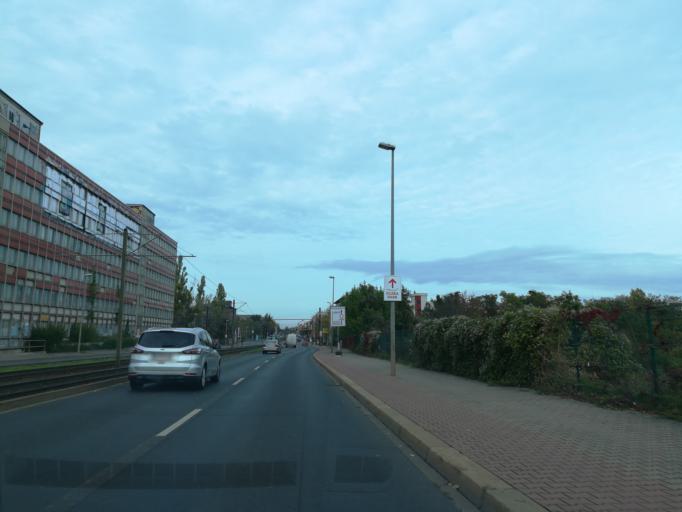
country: DE
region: Saxony-Anhalt
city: Magdeburg
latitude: 52.1213
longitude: 11.6068
